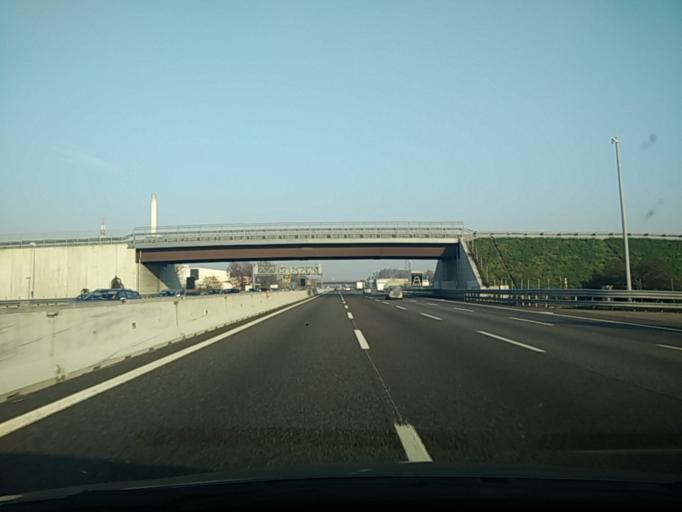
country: IT
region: Lombardy
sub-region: Provincia di Bergamo
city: Brembate
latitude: 45.6119
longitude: 9.5496
